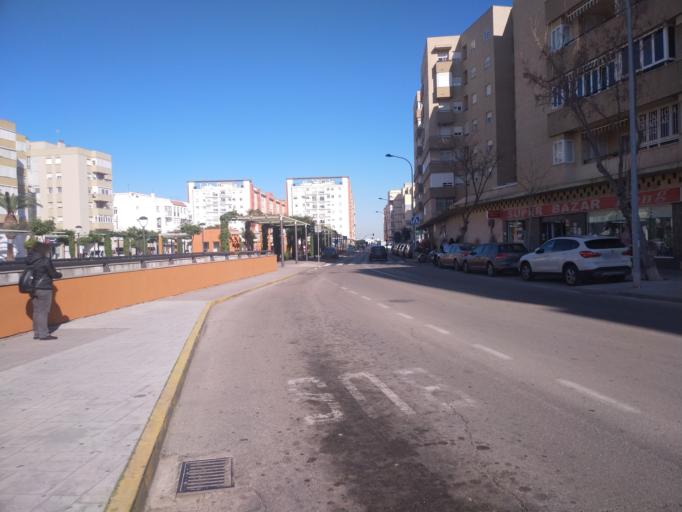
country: ES
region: Andalusia
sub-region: Provincia de Cadiz
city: San Fernando
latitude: 36.4682
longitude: -6.2001
